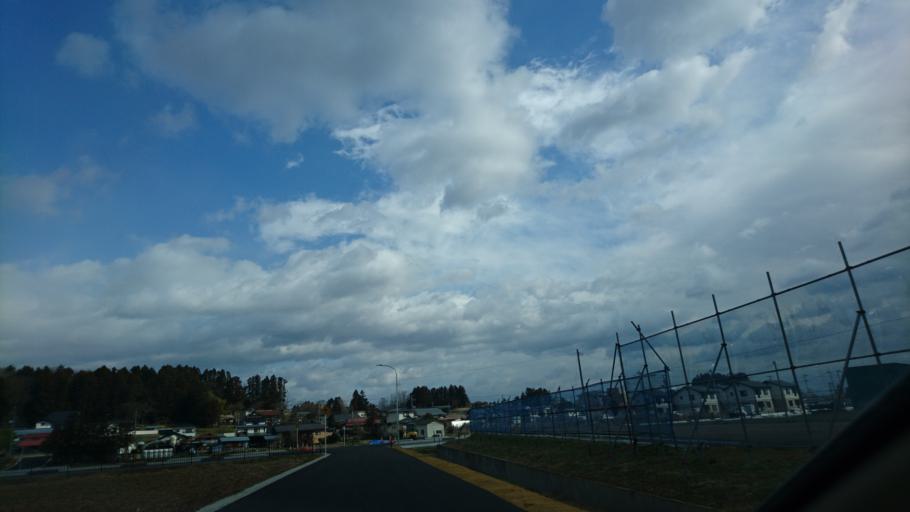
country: JP
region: Iwate
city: Ichinoseki
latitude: 38.7714
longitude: 141.1152
